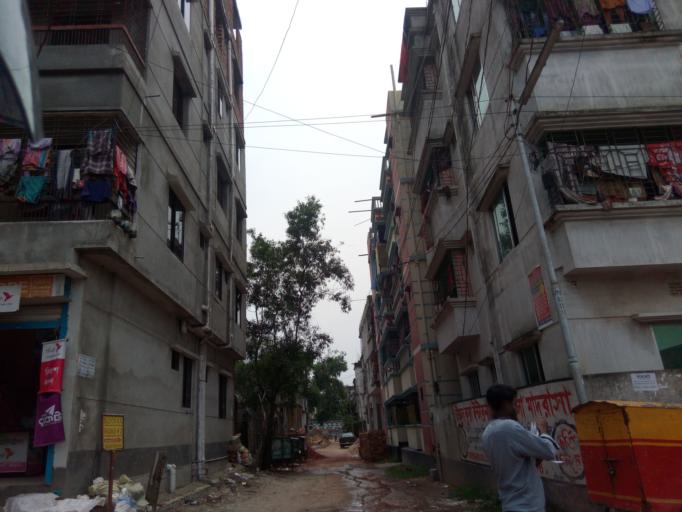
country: BD
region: Dhaka
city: Azimpur
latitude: 23.7447
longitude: 90.3491
